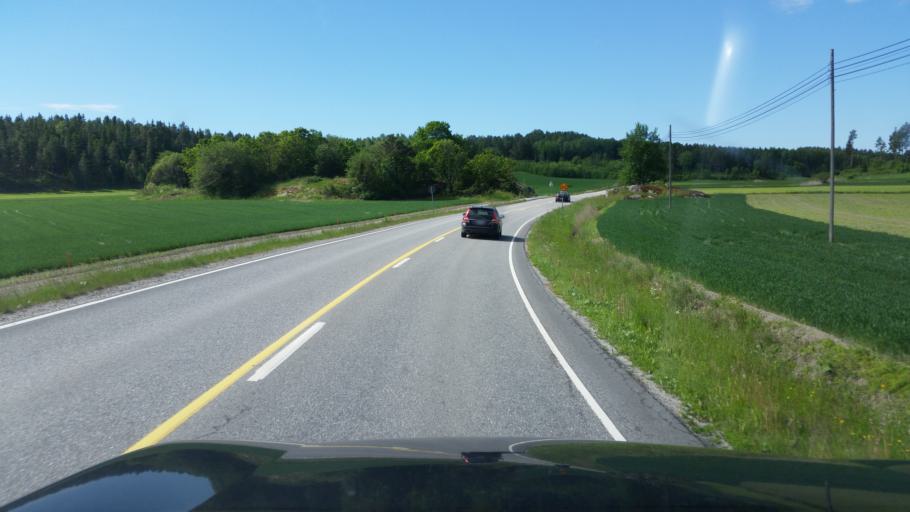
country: FI
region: Varsinais-Suomi
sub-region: Aboland-Turunmaa
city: Laensi-Turunmaa
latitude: 60.2797
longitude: 22.2447
